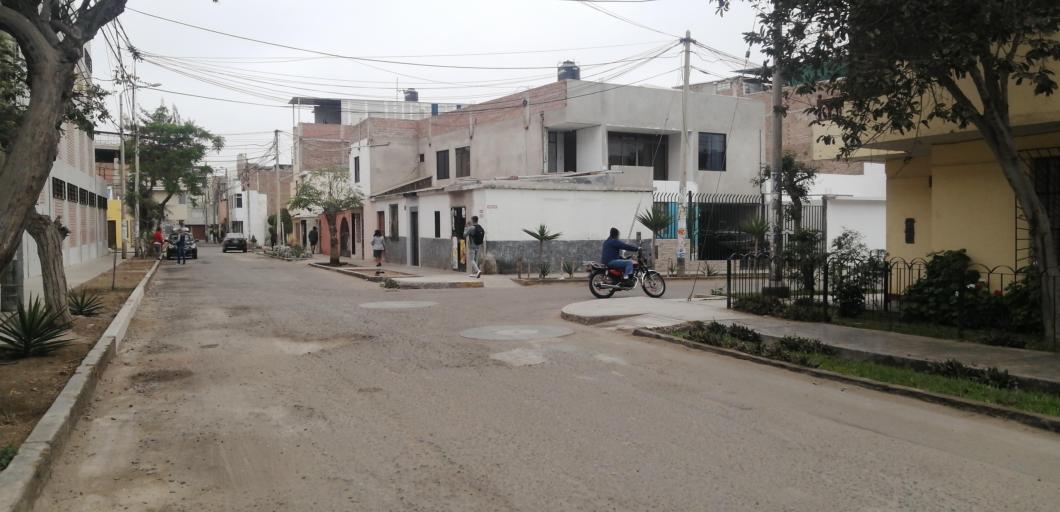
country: PE
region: La Libertad
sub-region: Provincia de Trujillo
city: Trujillo
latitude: -8.1042
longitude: -79.0417
